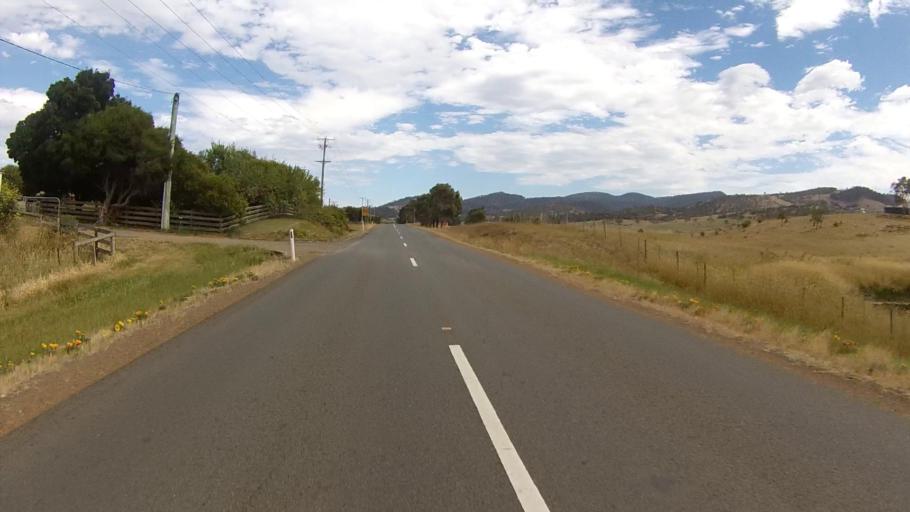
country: AU
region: Tasmania
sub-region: Brighton
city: Old Beach
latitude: -42.6943
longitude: 147.3484
